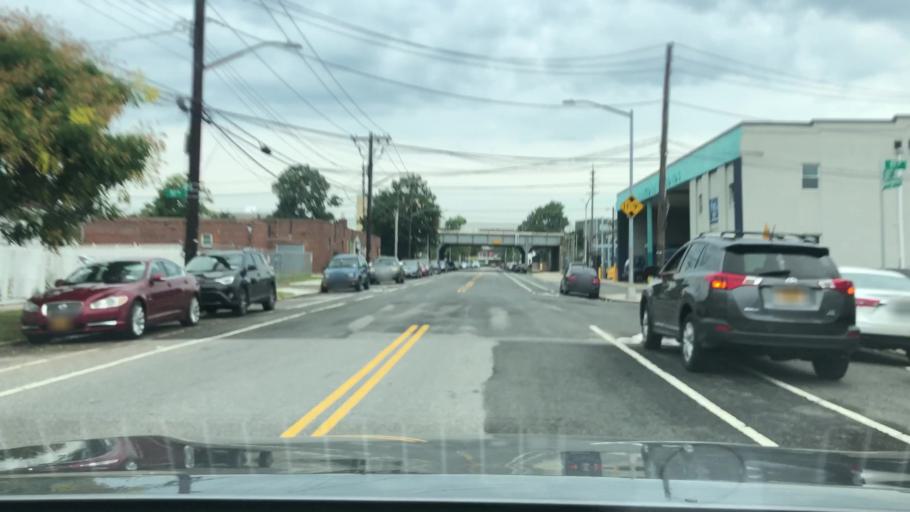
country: US
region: New York
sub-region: Nassau County
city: Bellerose Terrace
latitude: 40.7174
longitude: -73.7315
